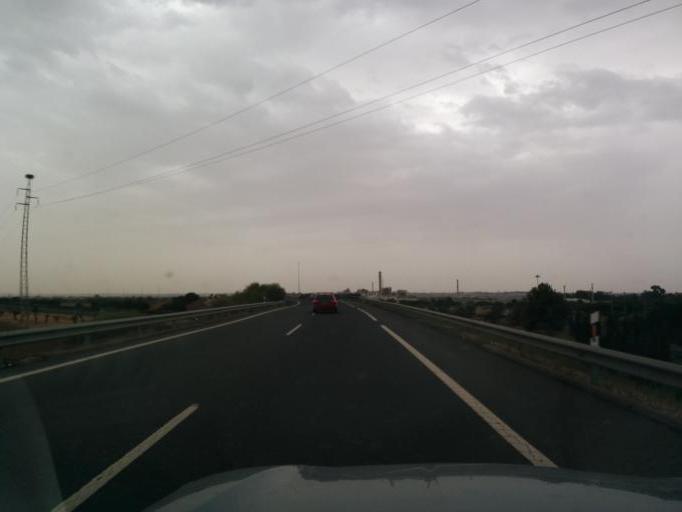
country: ES
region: Andalusia
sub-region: Provincia de Huelva
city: San Juan del Puerto
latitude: 37.3123
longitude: -6.8817
